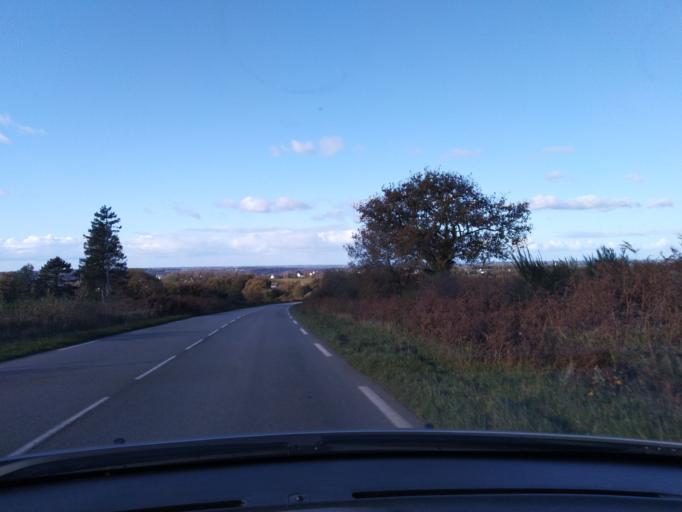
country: FR
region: Brittany
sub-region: Departement du Finistere
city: Guerlesquin
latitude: 48.5623
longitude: -3.6023
